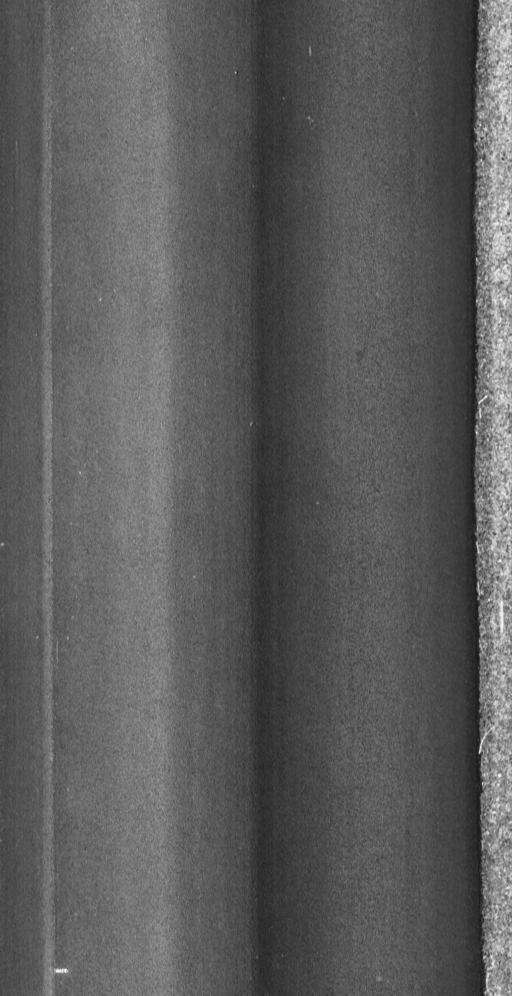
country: US
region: Vermont
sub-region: Washington County
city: Montpelier
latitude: 44.3322
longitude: -72.5260
